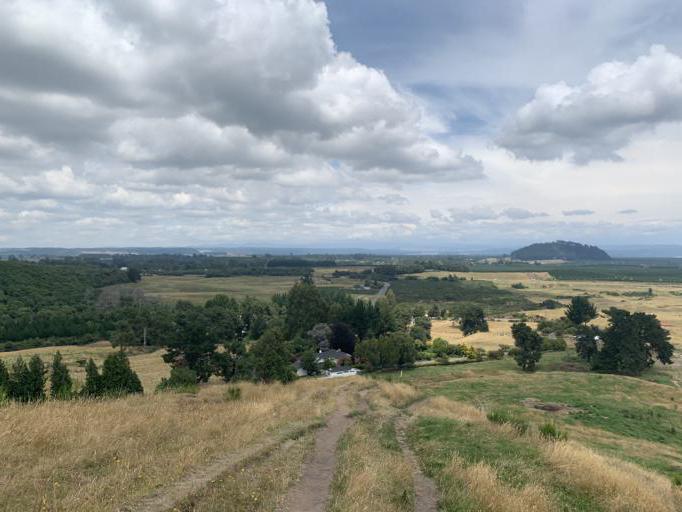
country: NZ
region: Waikato
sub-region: Taupo District
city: Taupo
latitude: -38.7016
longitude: 176.1422
